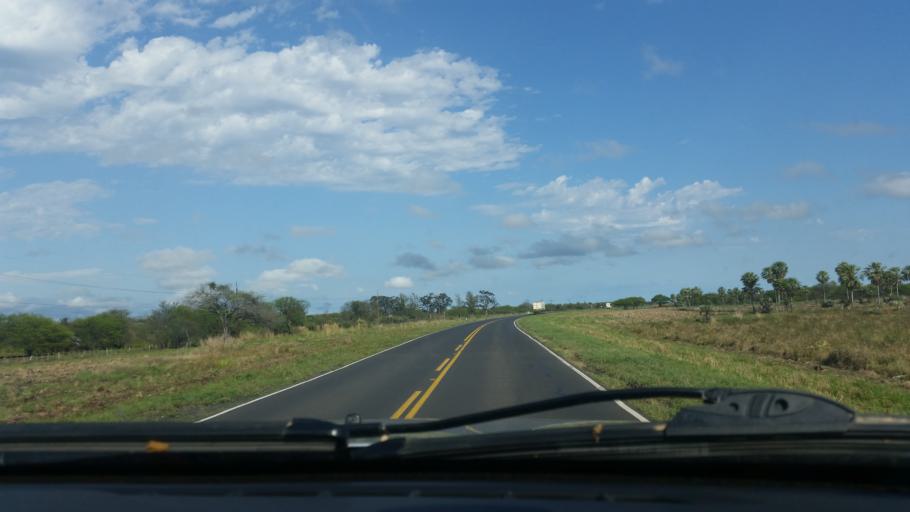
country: PY
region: Presidente Hayes
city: Benjamin Aceval
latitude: -24.9204
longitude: -57.6000
